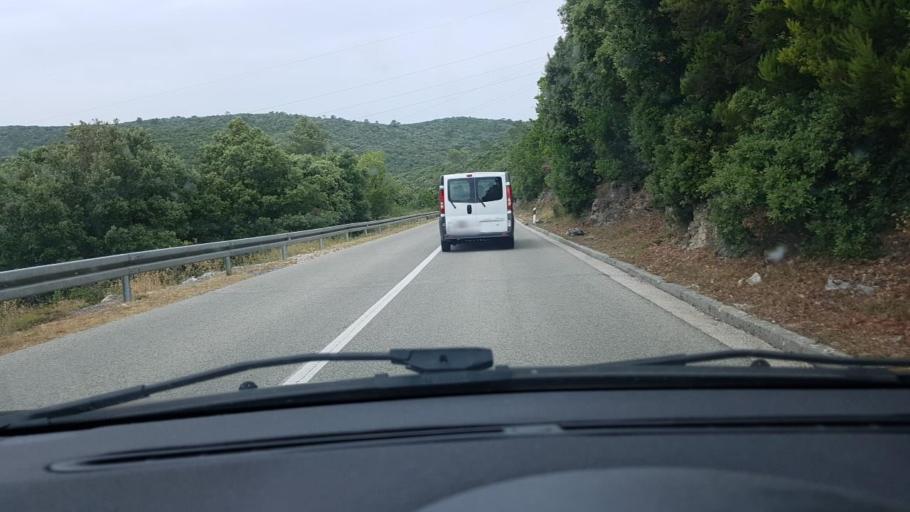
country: HR
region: Dubrovacko-Neretvanska
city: Smokvica
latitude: 42.9457
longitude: 17.0028
